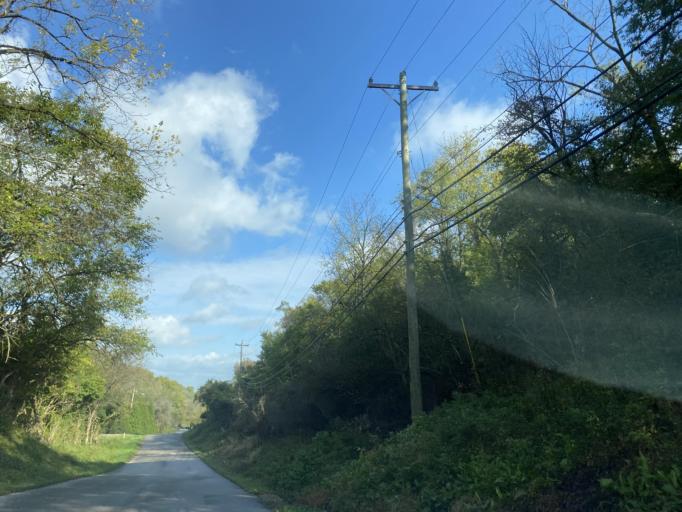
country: US
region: Kentucky
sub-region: Campbell County
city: Cold Spring
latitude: 39.0258
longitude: -84.4192
